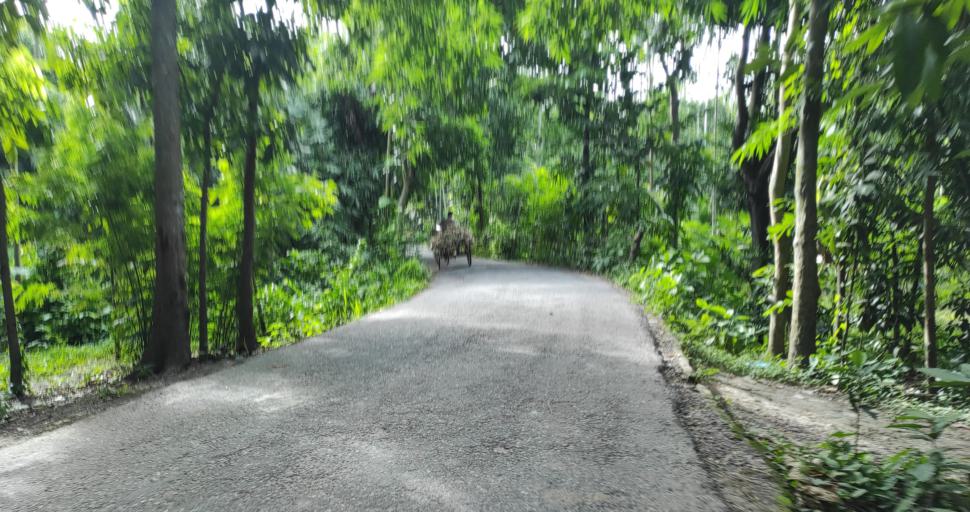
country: BD
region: Barisal
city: Gaurnadi
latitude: 22.8935
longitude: 90.1869
